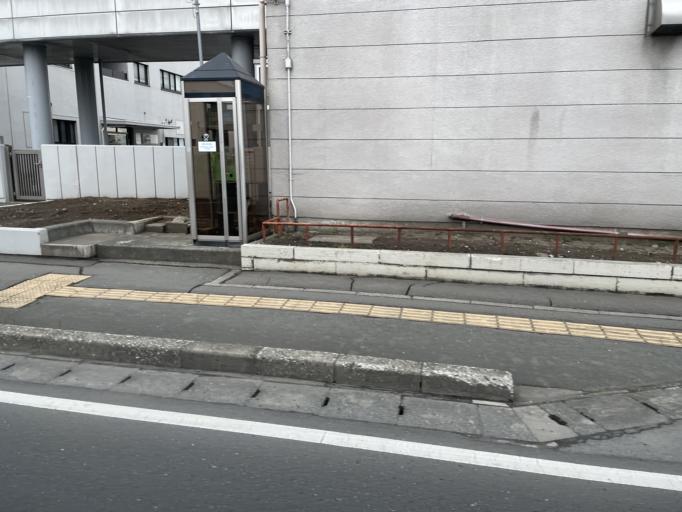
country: JP
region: Aomori
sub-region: Hachinohe Shi
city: Uchimaru
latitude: 40.5144
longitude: 141.4992
